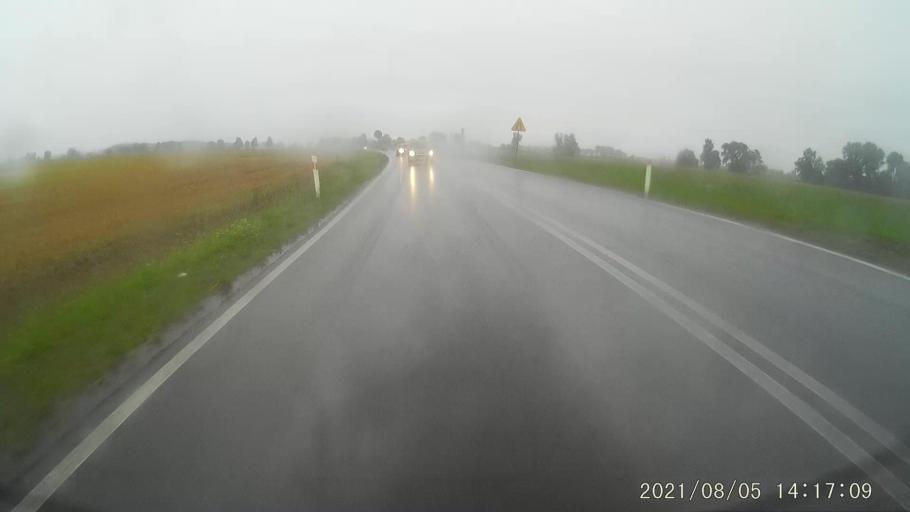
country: PL
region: Opole Voivodeship
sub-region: Powiat prudnicki
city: Biala
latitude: 50.4595
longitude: 17.7106
